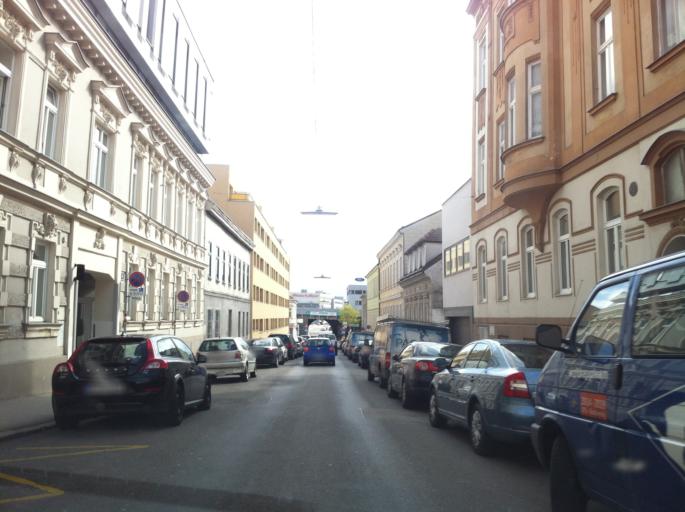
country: AT
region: Lower Austria
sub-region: Politischer Bezirk Modling
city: Perchtoldsdorf
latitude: 48.1950
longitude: 16.2815
